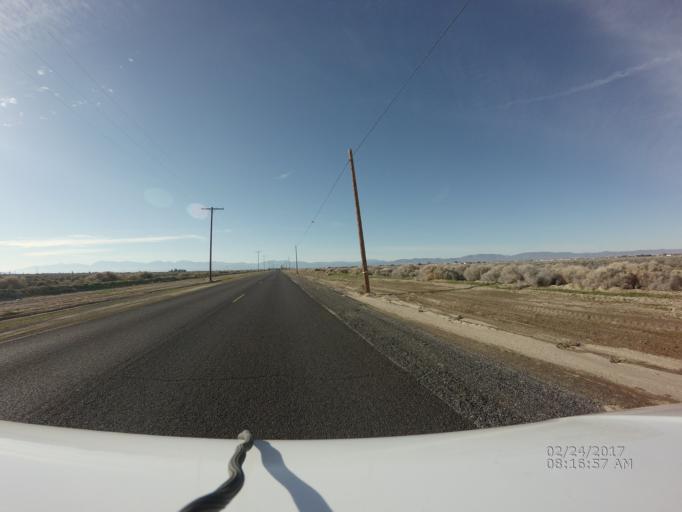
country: US
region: California
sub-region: Los Angeles County
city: Lancaster
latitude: 34.7243
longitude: -118.0412
